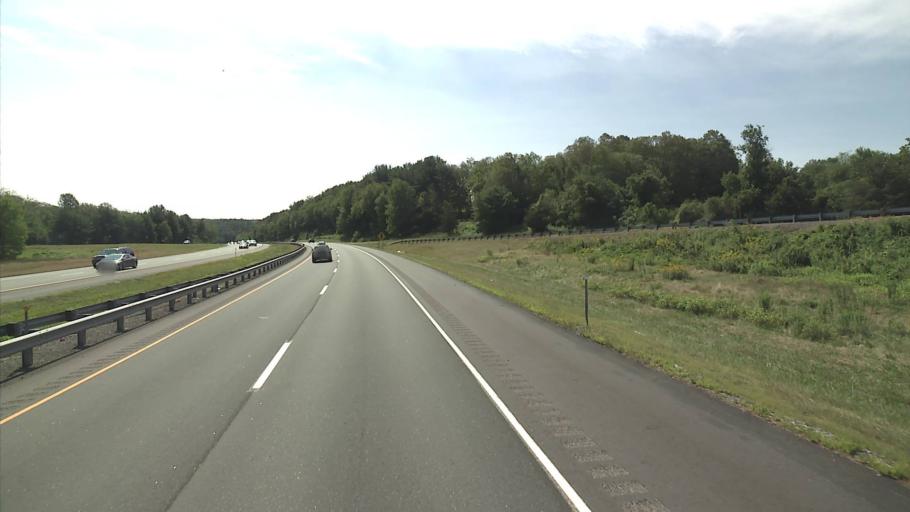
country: US
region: Connecticut
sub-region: Hartford County
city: Terramuggus
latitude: 41.6096
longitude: -72.4326
